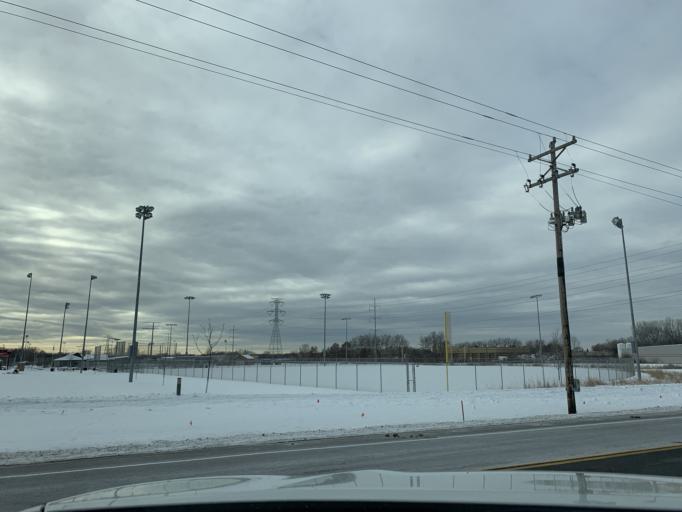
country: US
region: Minnesota
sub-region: Anoka County
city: Andover
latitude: 45.1811
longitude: -93.2923
